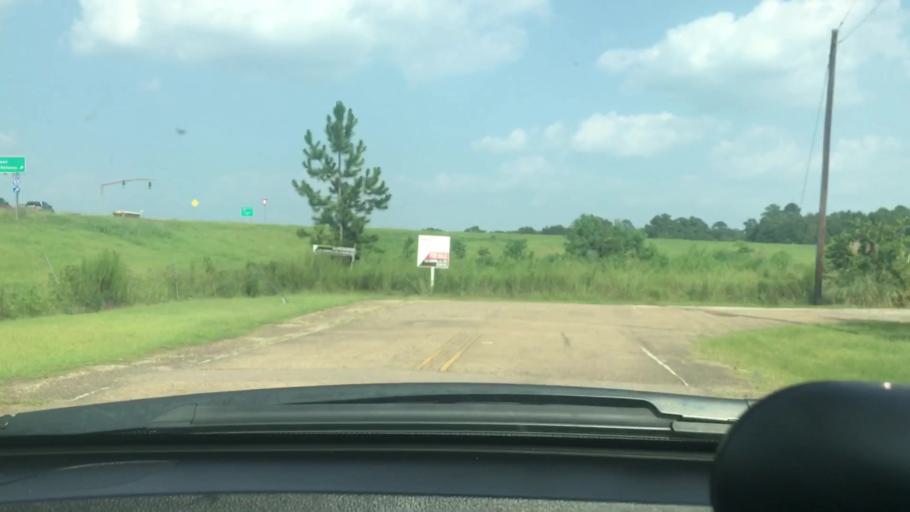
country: US
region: Louisiana
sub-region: Tangipahoa Parish
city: Natalbany
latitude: 30.5186
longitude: -90.5061
